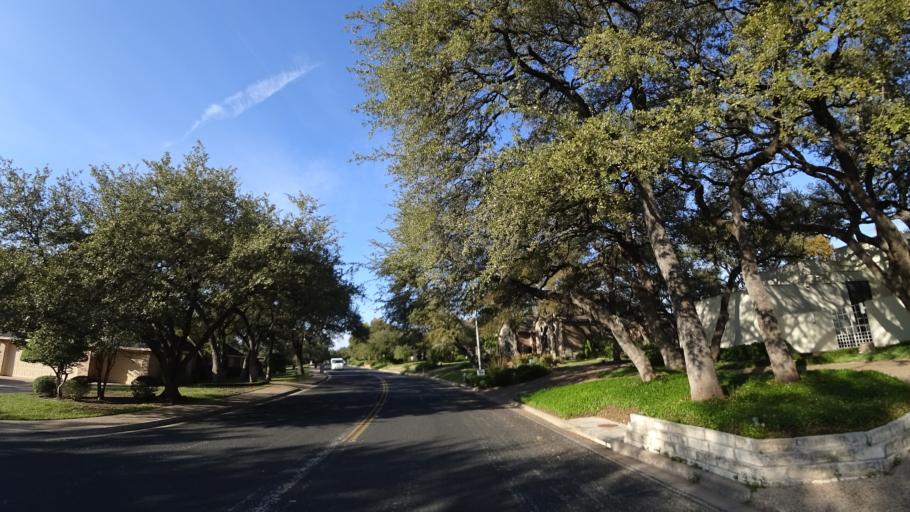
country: US
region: Texas
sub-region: Williamson County
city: Anderson Mill
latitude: 30.4309
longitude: -97.8106
